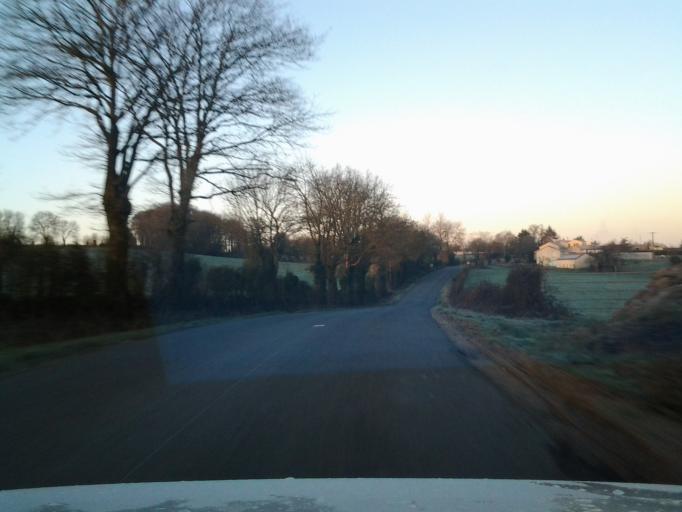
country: FR
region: Pays de la Loire
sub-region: Departement de la Vendee
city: Chambretaud
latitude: 46.9258
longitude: -0.9967
